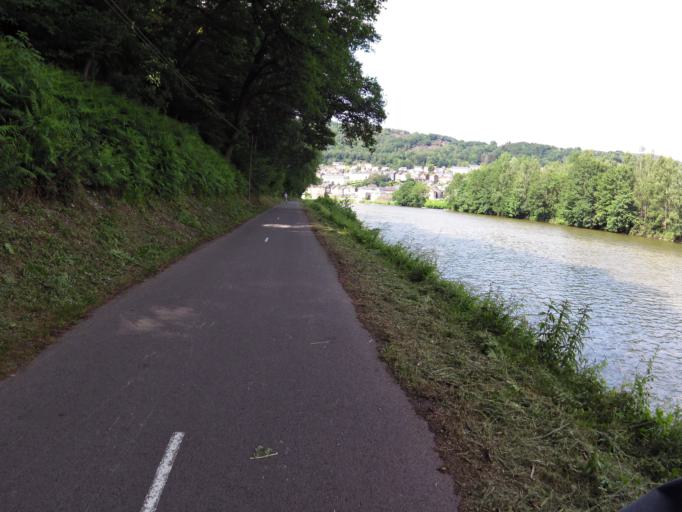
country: FR
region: Champagne-Ardenne
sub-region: Departement des Ardennes
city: Montherme
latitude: 49.8814
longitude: 4.7371
